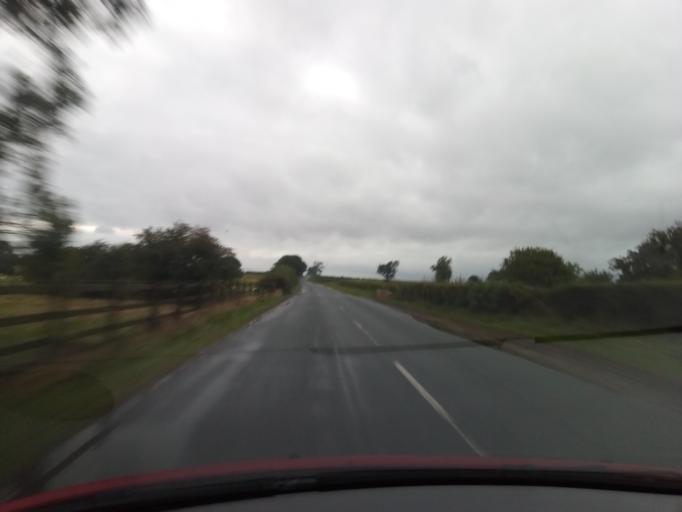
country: GB
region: England
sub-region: Darlington
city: High Coniscliffe
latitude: 54.5004
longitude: -1.6708
